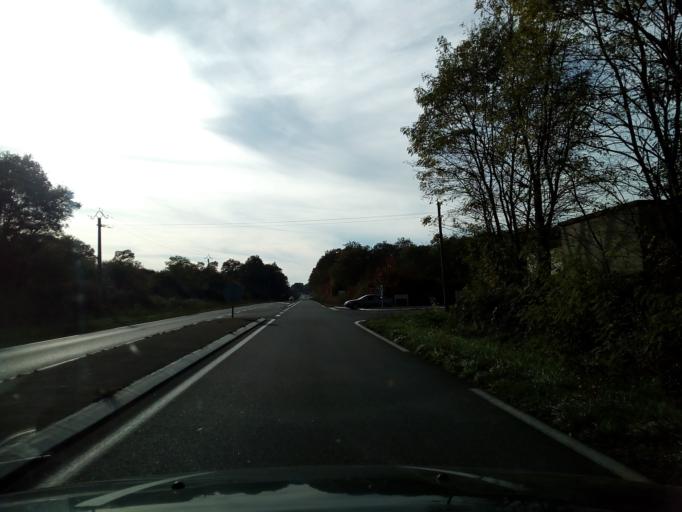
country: FR
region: Poitou-Charentes
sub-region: Departement de la Charente
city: Brigueuil
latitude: 46.0975
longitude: 0.8546
